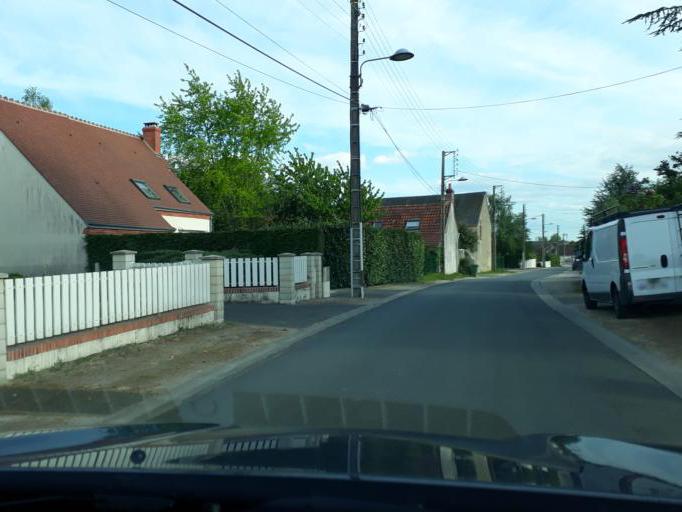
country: FR
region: Centre
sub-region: Departement du Loiret
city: Ingre
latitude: 47.9147
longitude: 1.8404
